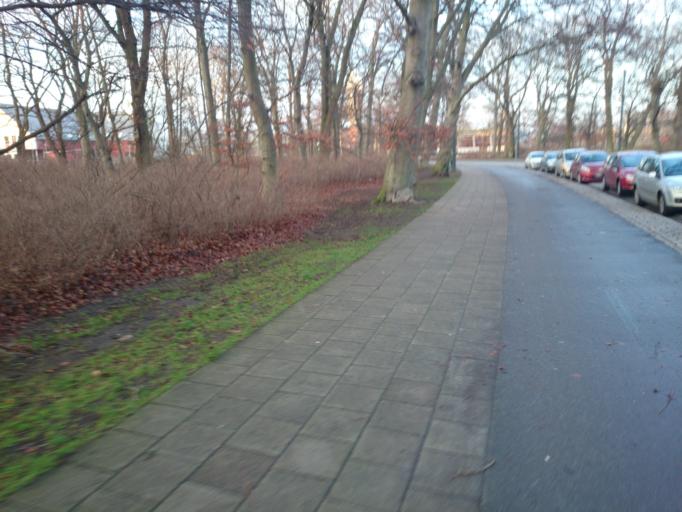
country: SE
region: Skane
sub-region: Malmo
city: Malmoe
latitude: 55.6023
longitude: 12.9841
